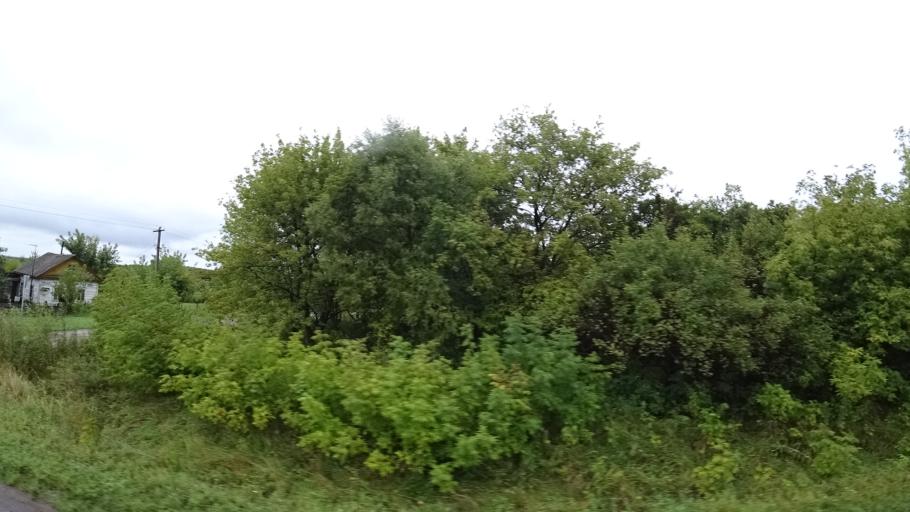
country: RU
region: Primorskiy
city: Monastyrishche
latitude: 44.2728
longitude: 132.4248
